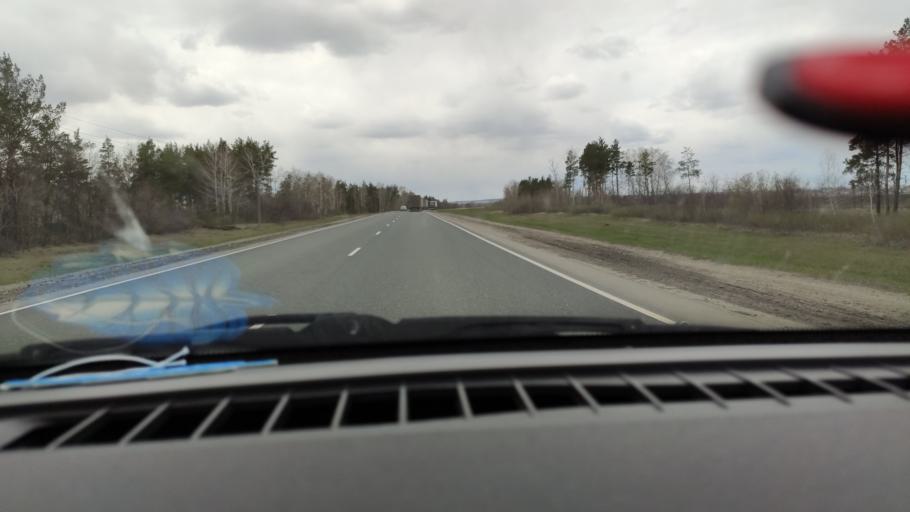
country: RU
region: Saratov
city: Sennoy
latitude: 52.1510
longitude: 46.9927
